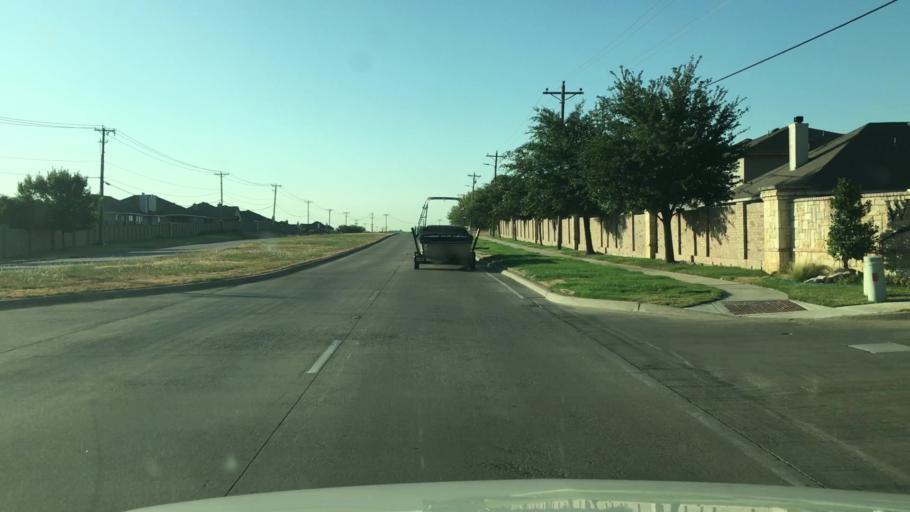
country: US
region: Texas
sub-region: Johnson County
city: Burleson
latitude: 32.5352
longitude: -97.3565
